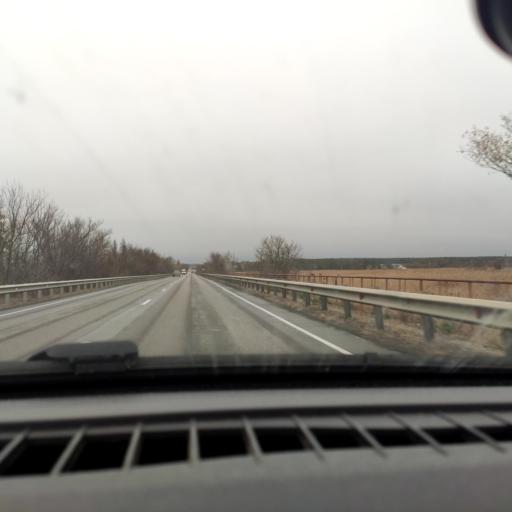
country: RU
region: Voronezj
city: Ostrogozhsk
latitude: 51.0353
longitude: 38.9842
